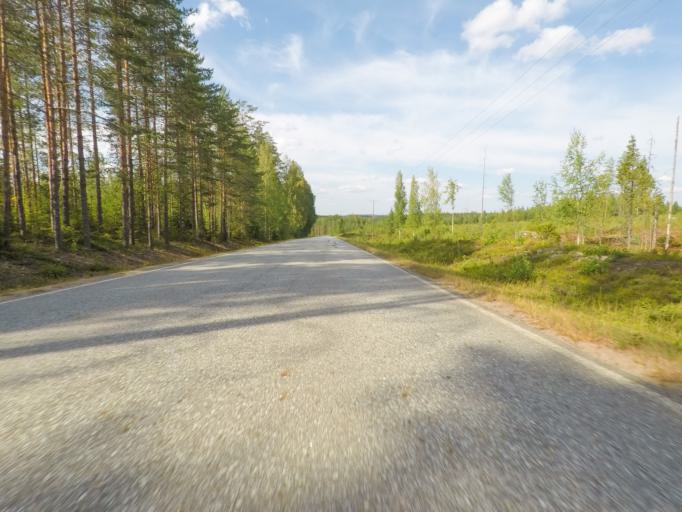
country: FI
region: Southern Savonia
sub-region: Savonlinna
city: Sulkava
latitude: 61.7142
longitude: 28.2101
